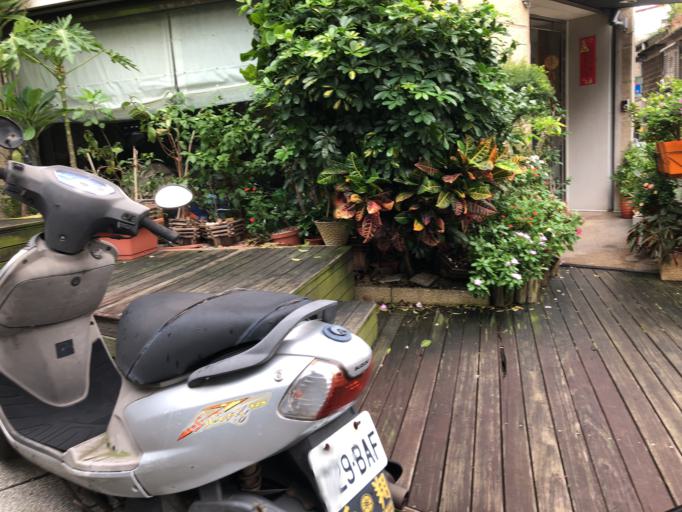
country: TW
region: Taiwan
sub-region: Taoyuan
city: Taoyuan
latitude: 24.9505
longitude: 121.3511
